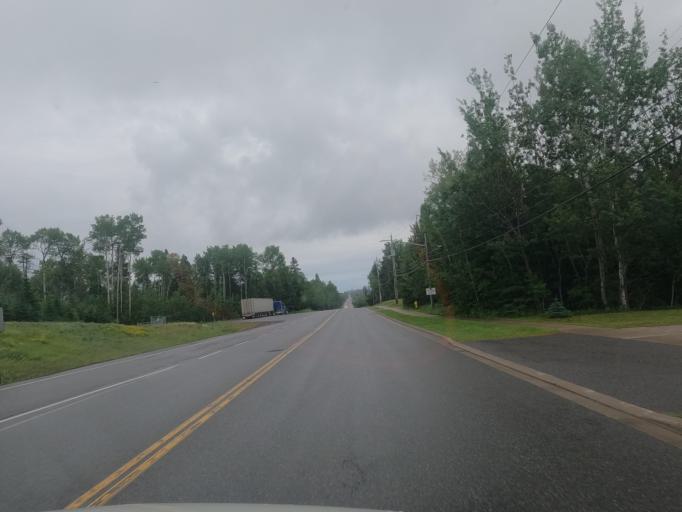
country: CA
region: Ontario
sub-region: Thunder Bay District
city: Thunder Bay
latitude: 48.4816
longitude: -89.1823
